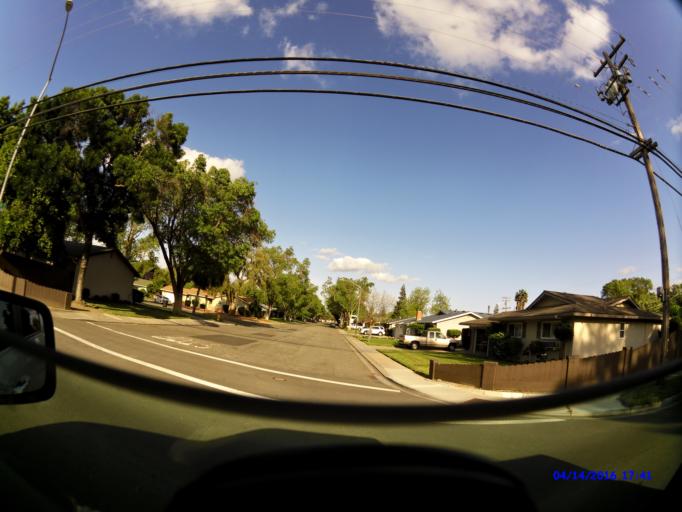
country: US
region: California
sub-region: Stanislaus County
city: Modesto
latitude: 37.6619
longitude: -120.9575
